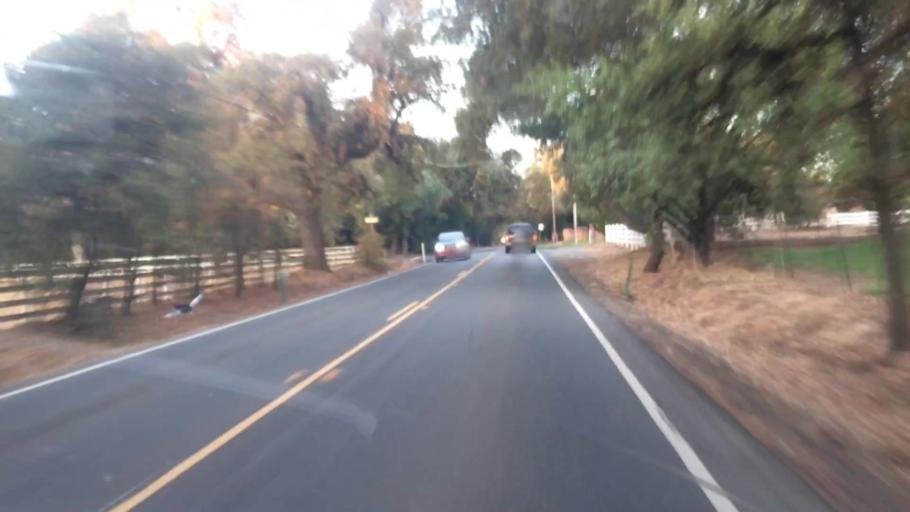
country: US
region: California
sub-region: Sacramento County
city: Vineyard
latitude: 38.4383
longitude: -121.3107
